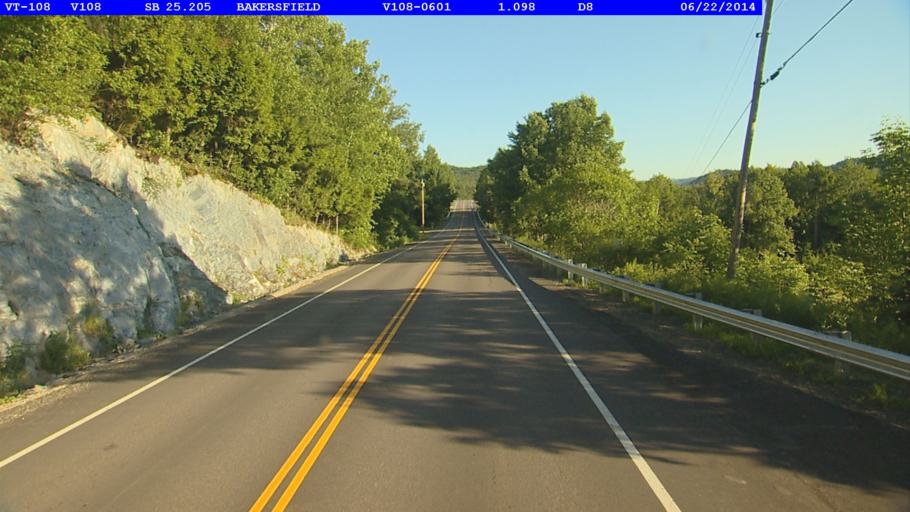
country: US
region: Vermont
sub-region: Franklin County
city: Enosburg Falls
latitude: 44.7490
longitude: -72.8237
